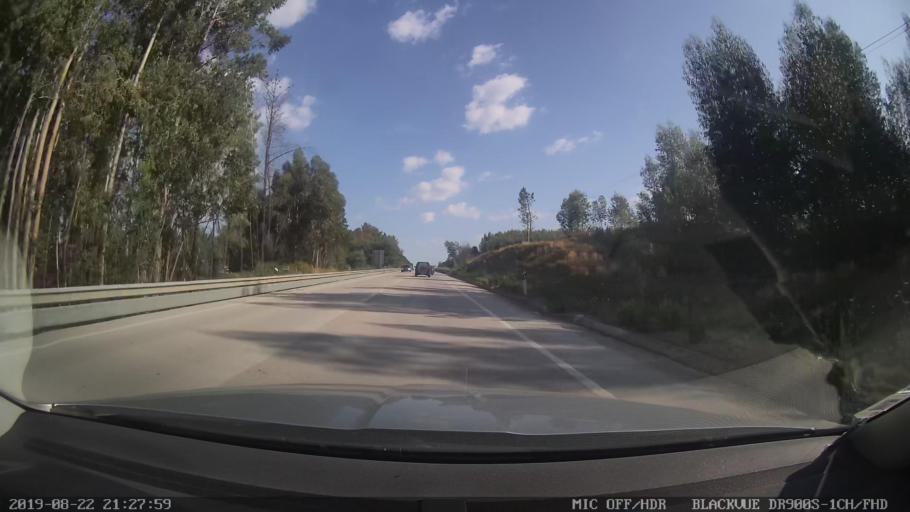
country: PT
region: Leiria
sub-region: Pedrogao Grande
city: Pedrogao Grande
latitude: 39.8864
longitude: -8.1205
